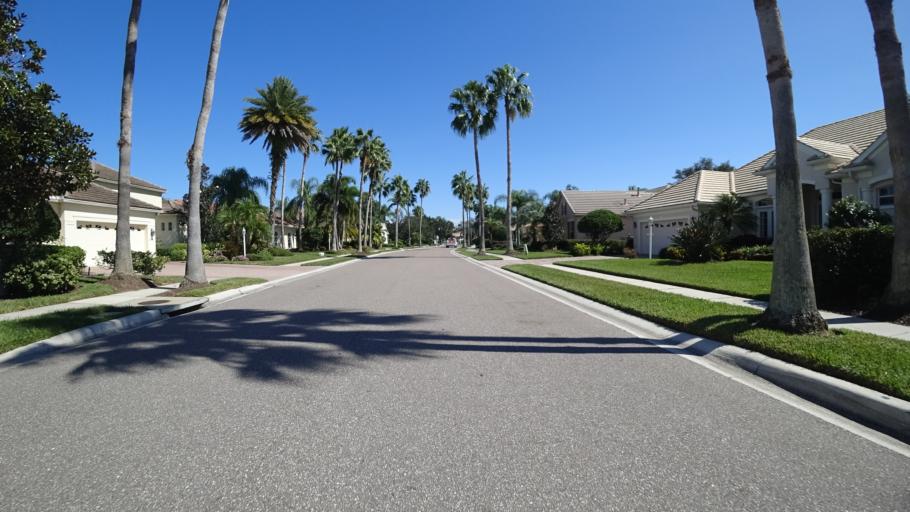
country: US
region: Florida
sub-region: Sarasota County
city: The Meadows
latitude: 27.3984
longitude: -82.4202
